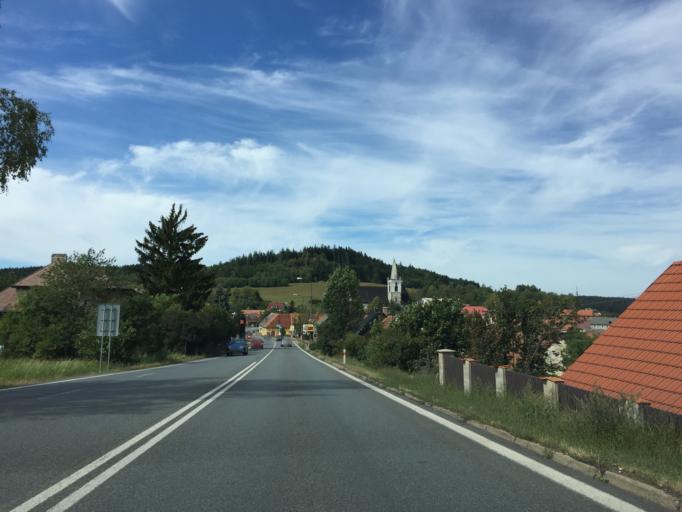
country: CZ
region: Central Bohemia
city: Votice
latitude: 49.5685
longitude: 14.6598
